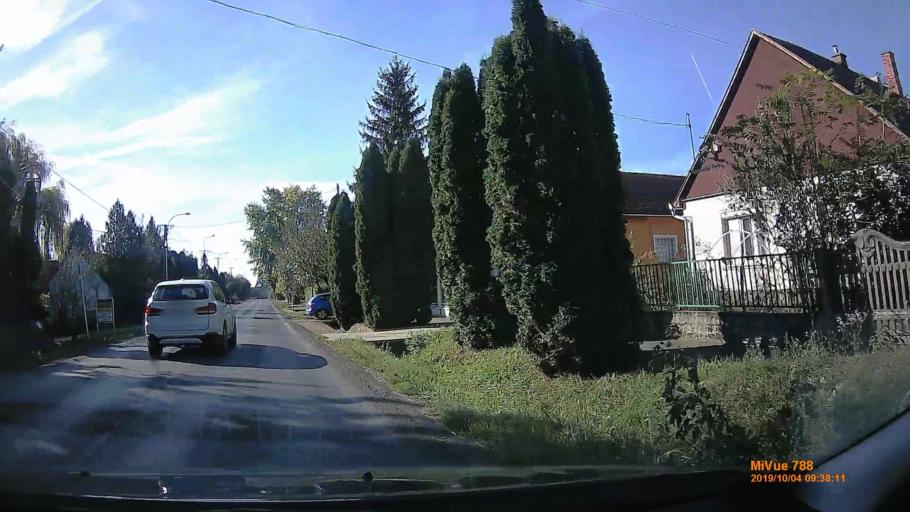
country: HU
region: Somogy
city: Kaposvar
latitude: 46.4611
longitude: 17.8050
